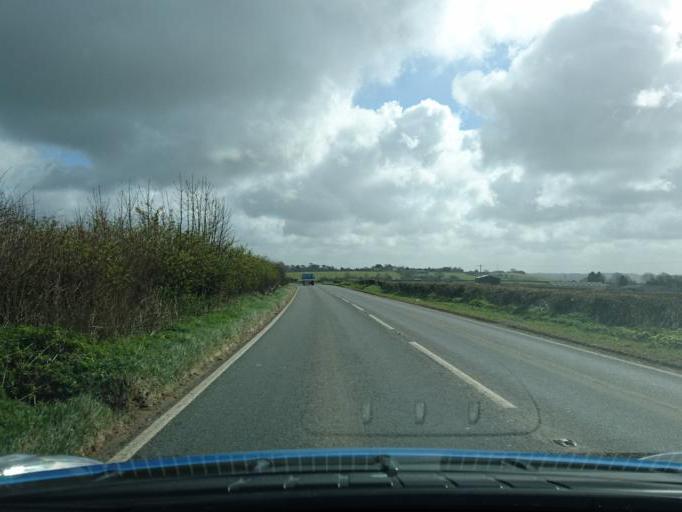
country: GB
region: England
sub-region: South Gloucestershire
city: Cold Ashton
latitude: 51.4520
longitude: -2.3789
